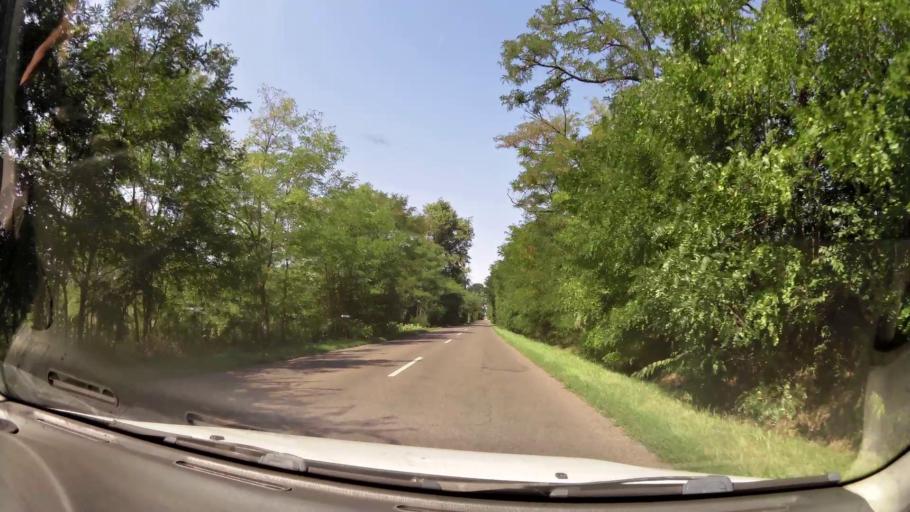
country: HU
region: Pest
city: Tapiosag
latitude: 47.3918
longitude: 19.6420
